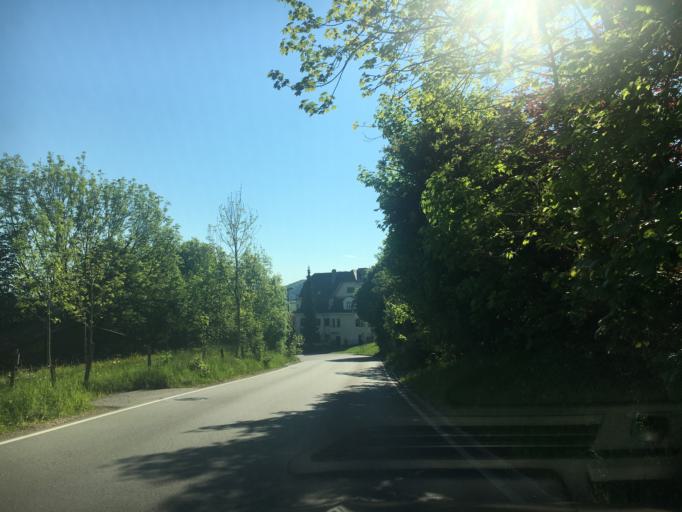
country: DE
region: Bavaria
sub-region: Upper Bavaria
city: Garching an der Alz
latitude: 48.1259
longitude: 12.5949
